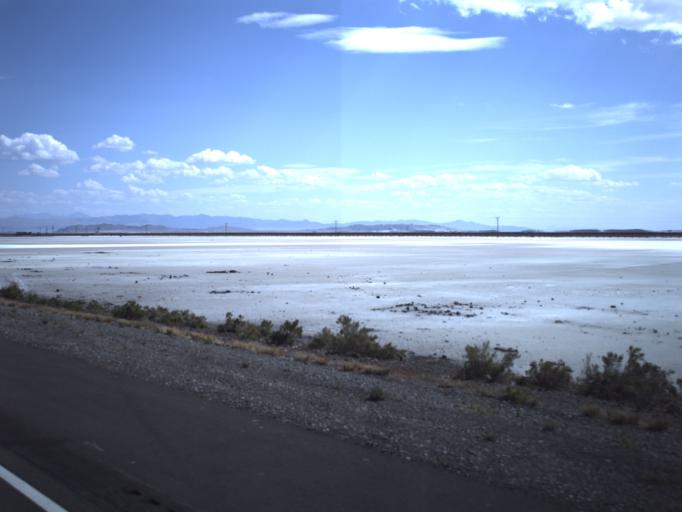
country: US
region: Utah
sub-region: Tooele County
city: Wendover
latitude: 40.7297
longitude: -113.4480
